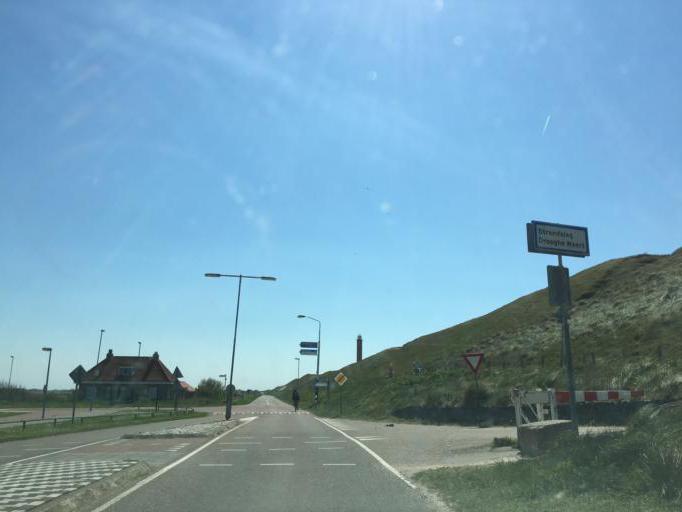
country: NL
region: North Holland
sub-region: Gemeente Den Helder
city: Den Helder
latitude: 52.8837
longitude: 4.7158
